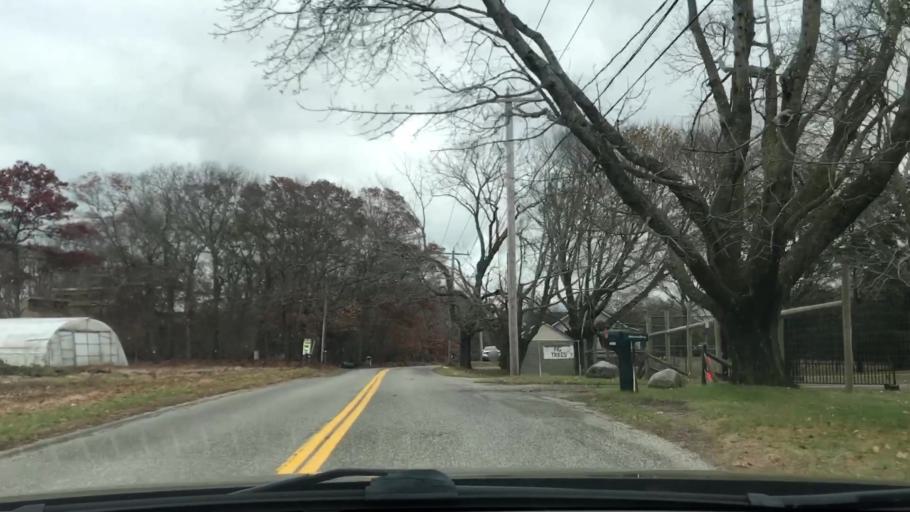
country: US
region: New York
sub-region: Suffolk County
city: Calverton
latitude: 40.9312
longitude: -72.7173
